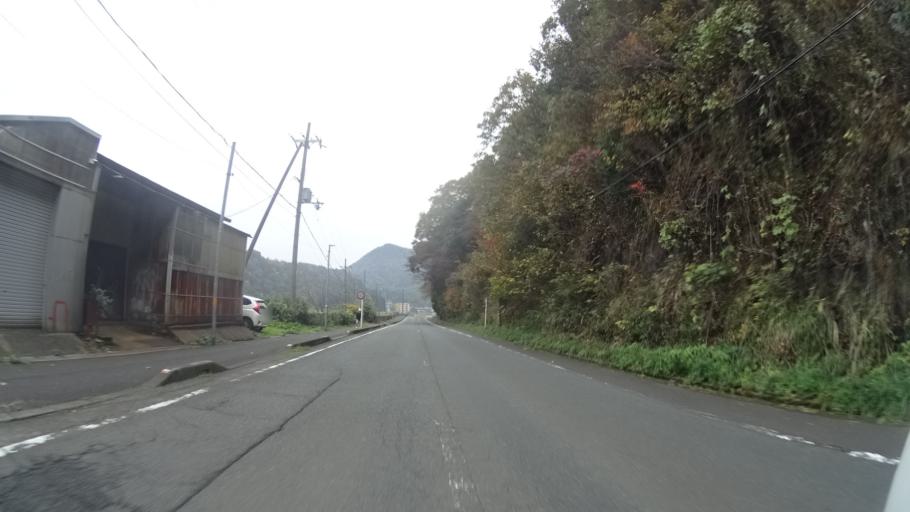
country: JP
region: Kyoto
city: Maizuru
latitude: 35.5046
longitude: 135.4346
